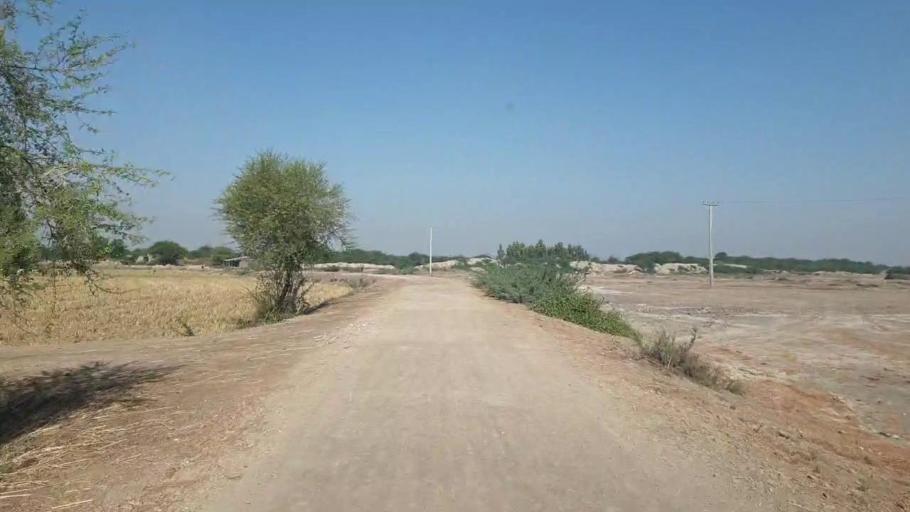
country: PK
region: Sindh
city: Talhar
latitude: 24.8012
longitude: 68.7905
